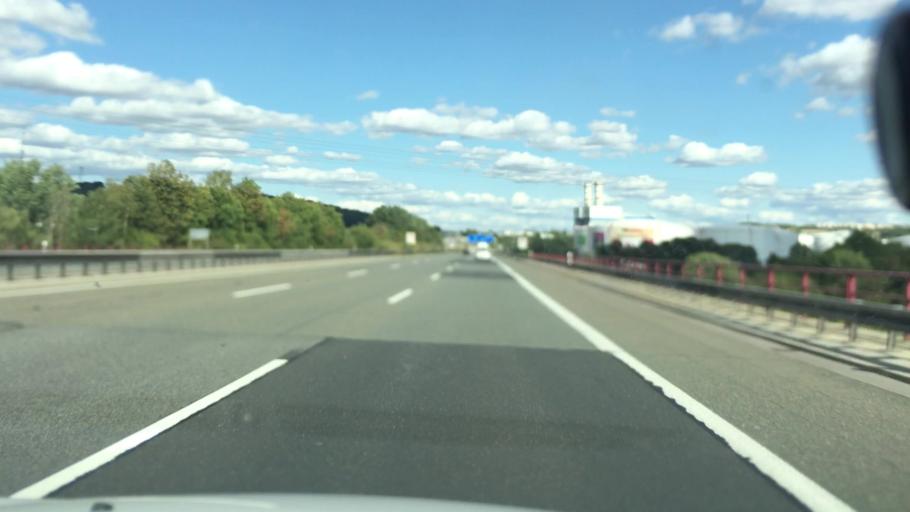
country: DE
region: Thuringia
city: Gera
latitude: 50.9074
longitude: 12.0532
